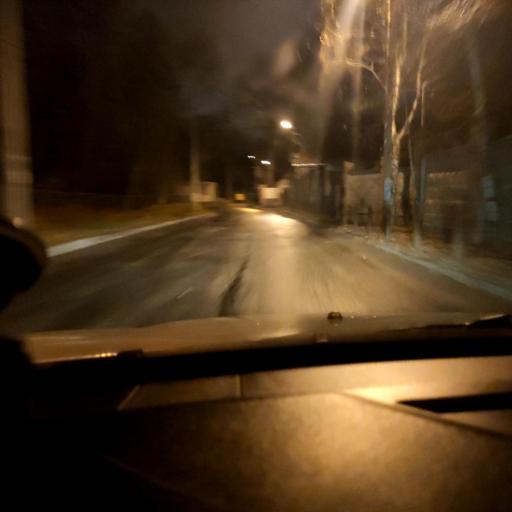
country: RU
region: Samara
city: Samara
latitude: 53.2866
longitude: 50.1988
